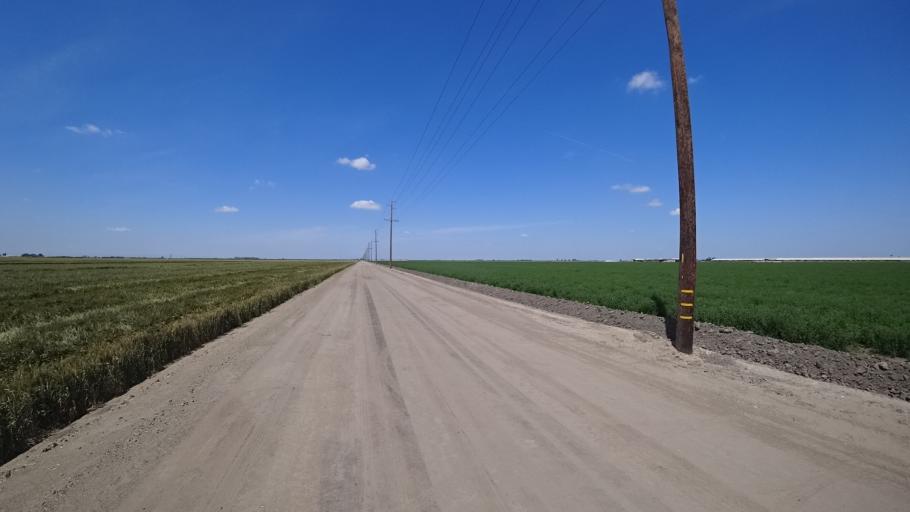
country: US
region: California
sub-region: Tulare County
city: Goshen
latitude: 36.3136
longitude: -119.5123
